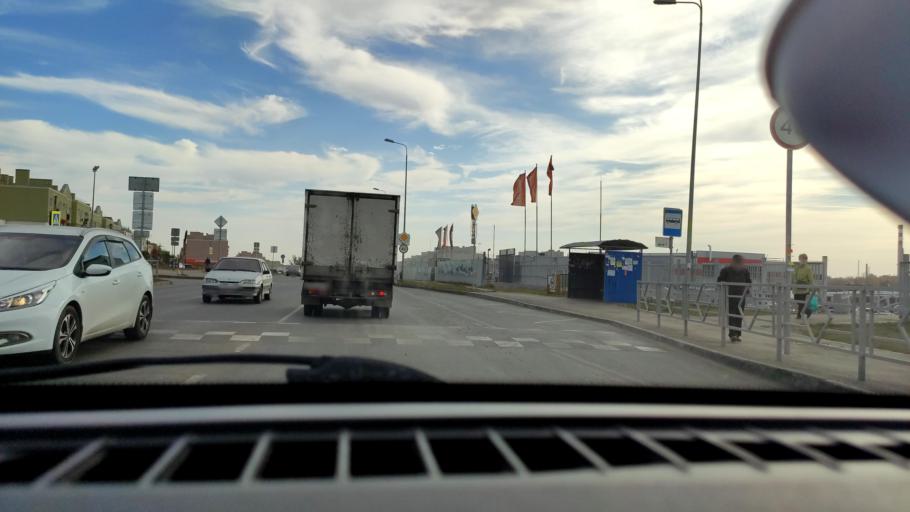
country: RU
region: Samara
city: Petra-Dubrava
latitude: 53.3167
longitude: 50.3038
